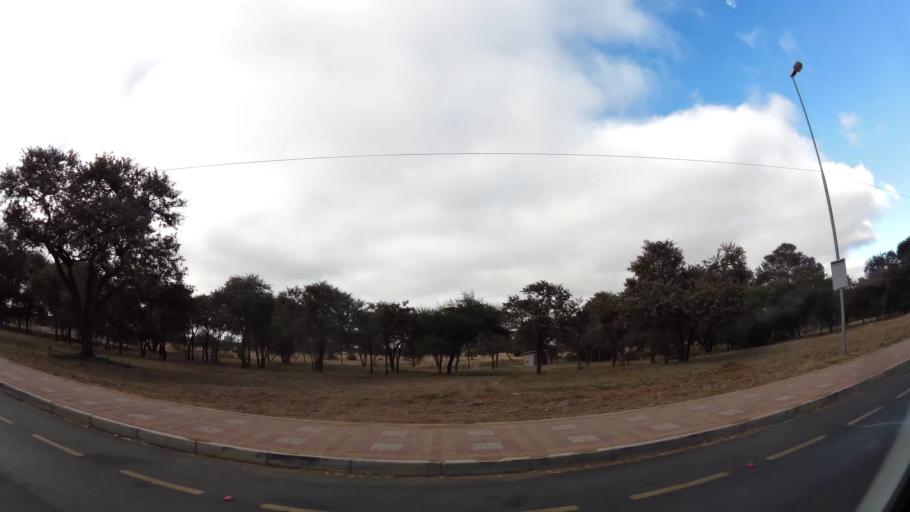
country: ZA
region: Limpopo
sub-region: Capricorn District Municipality
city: Polokwane
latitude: -23.9177
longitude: 29.4680
